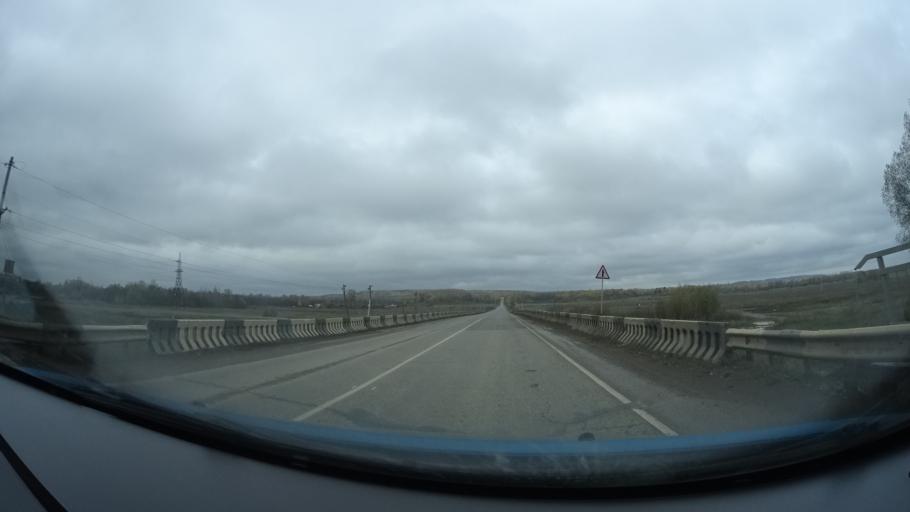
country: RU
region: Perm
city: Osa
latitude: 57.1799
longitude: 55.5687
